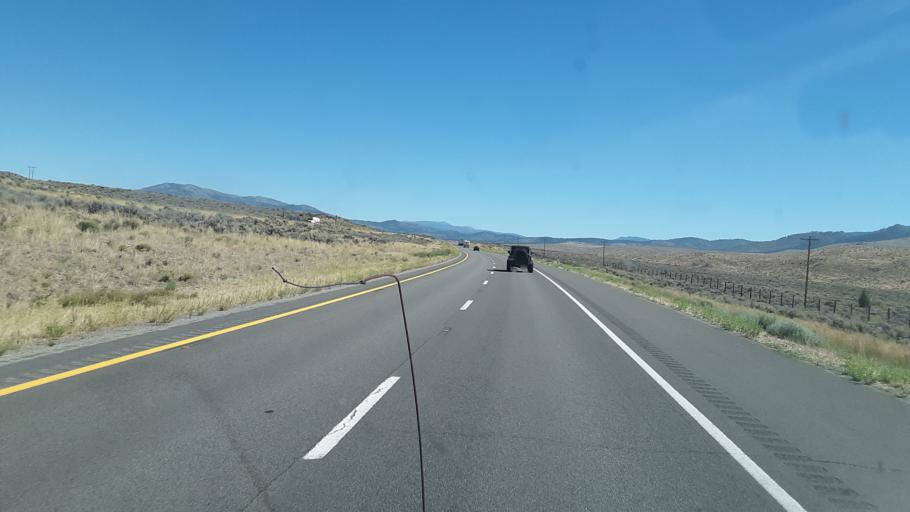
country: US
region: Nevada
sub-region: Washoe County
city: Cold Springs
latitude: 39.7183
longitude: -120.0382
